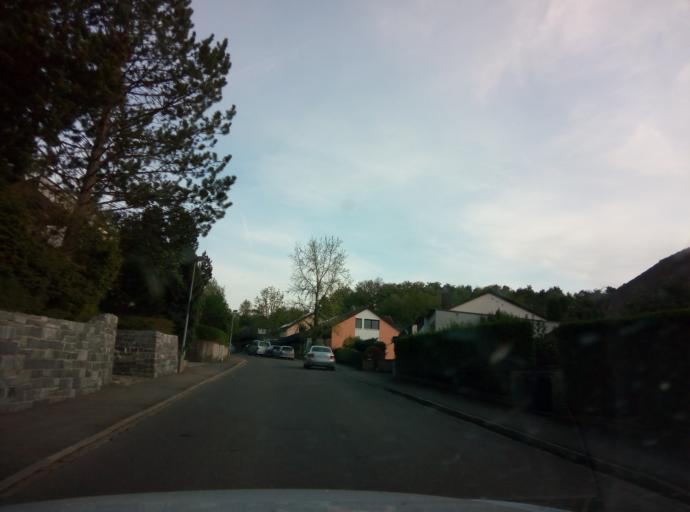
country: DE
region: Baden-Wuerttemberg
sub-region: Tuebingen Region
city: Tuebingen
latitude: 48.5144
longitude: 9.0326
